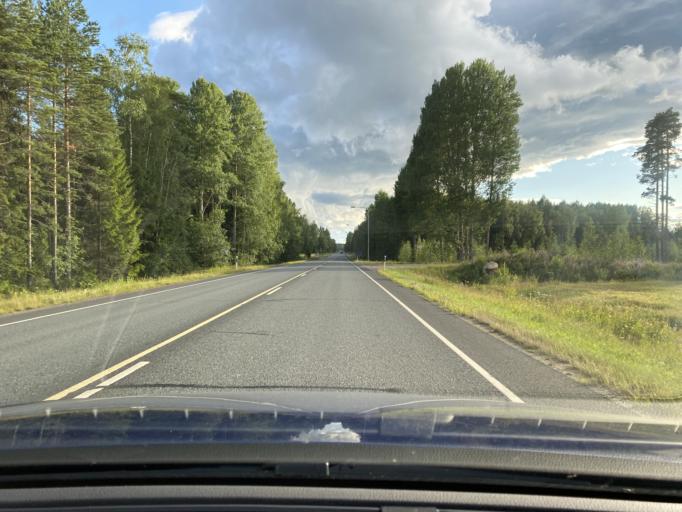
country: FI
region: Haeme
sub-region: Haemeenlinna
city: Renko
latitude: 60.8631
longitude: 24.1874
